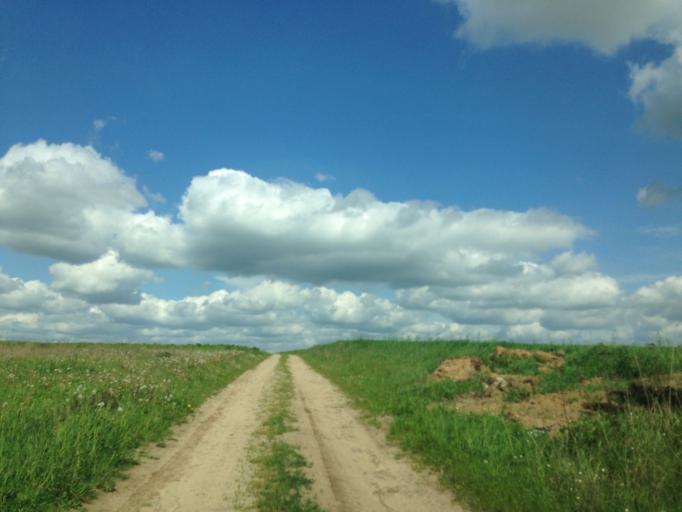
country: PL
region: Warmian-Masurian Voivodeship
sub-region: Powiat ostrodzki
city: Dabrowno
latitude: 53.3927
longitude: 20.1375
